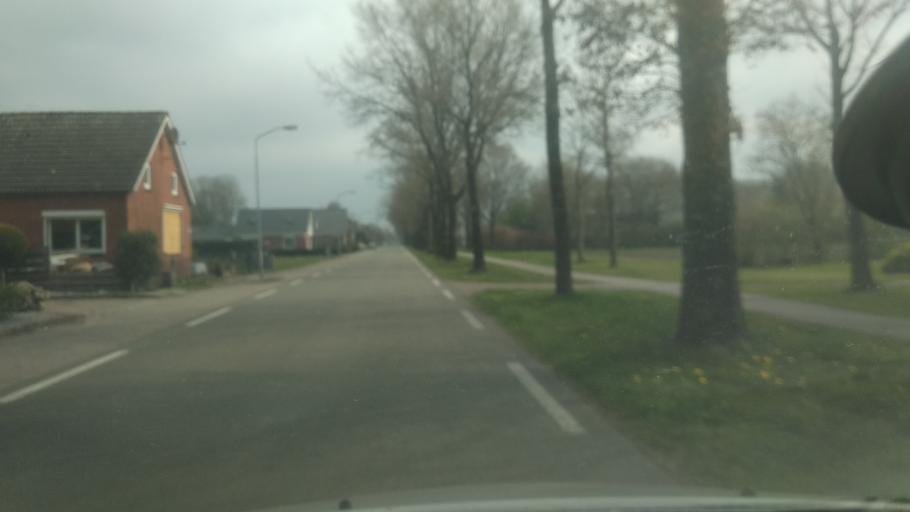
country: NL
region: Groningen
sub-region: Gemeente Stadskanaal
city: Stadskanaal
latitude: 52.9227
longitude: 6.9704
